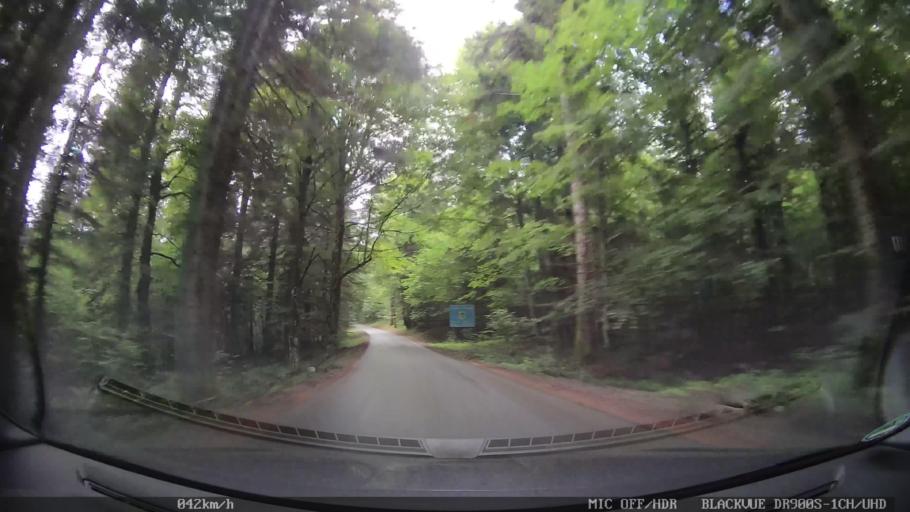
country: HR
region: Licko-Senjska
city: Jezerce
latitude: 44.9368
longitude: 15.5465
